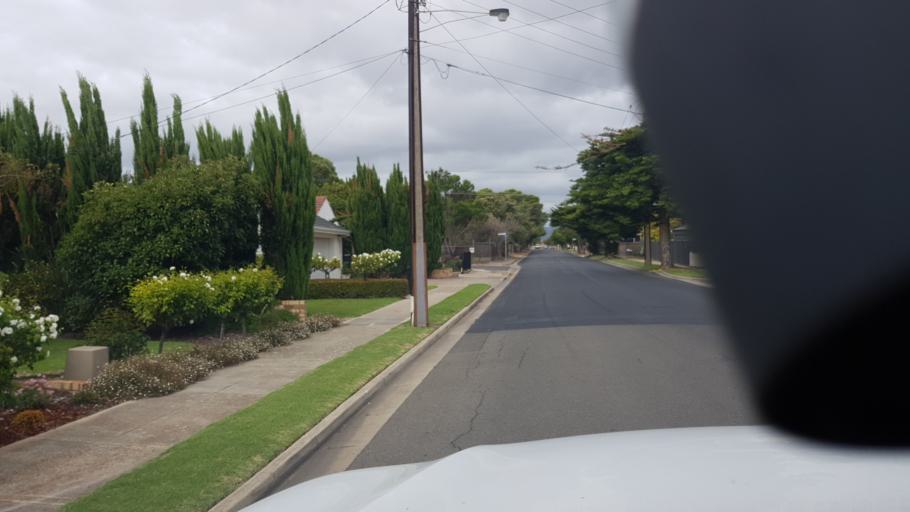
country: AU
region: South Australia
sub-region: Holdfast Bay
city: Glenelg East
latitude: -34.9651
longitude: 138.5209
